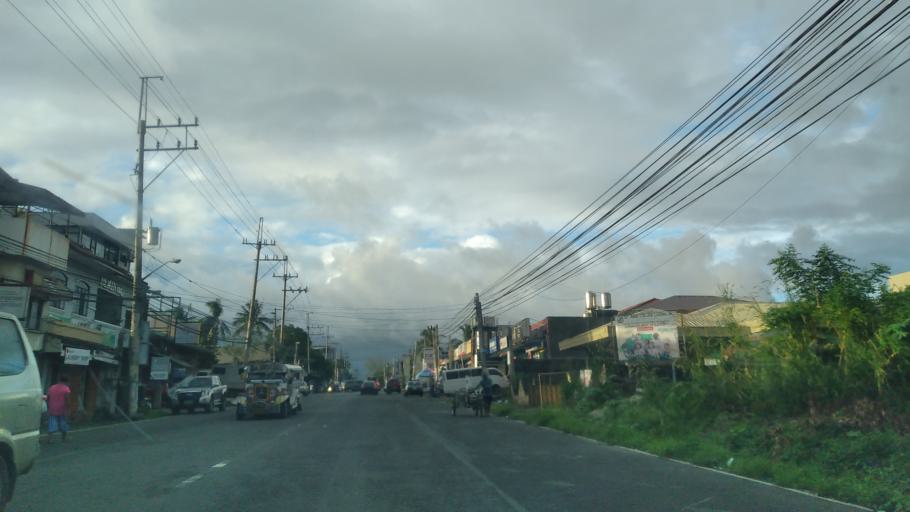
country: PH
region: Calabarzon
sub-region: Province of Quezon
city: Lucena
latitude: 13.9508
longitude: 121.6134
